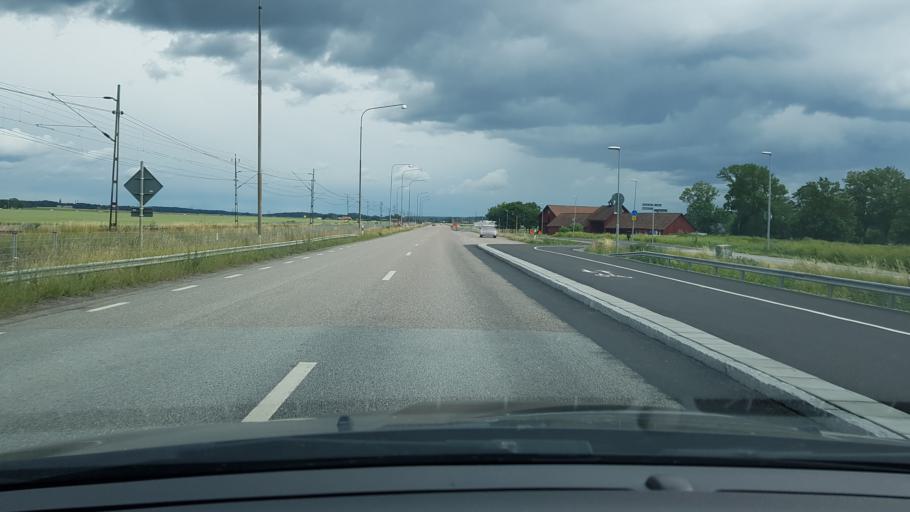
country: SE
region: Uppsala
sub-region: Uppsala Kommun
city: Uppsala
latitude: 59.8454
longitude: 17.6710
